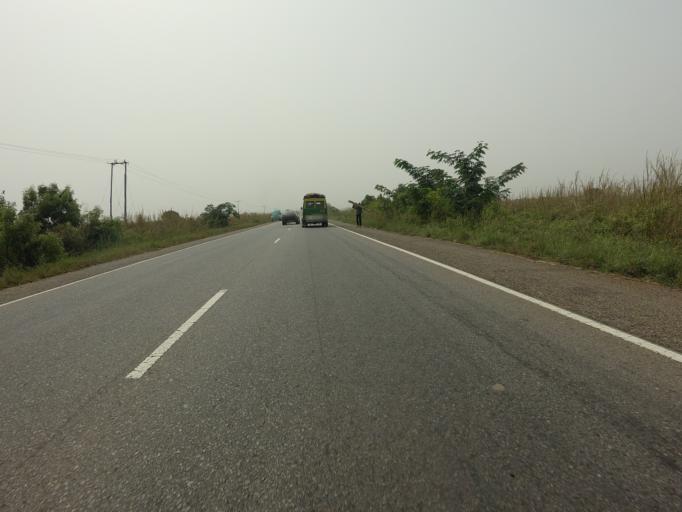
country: GH
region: Volta
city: Anloga
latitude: 5.9195
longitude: 0.5229
